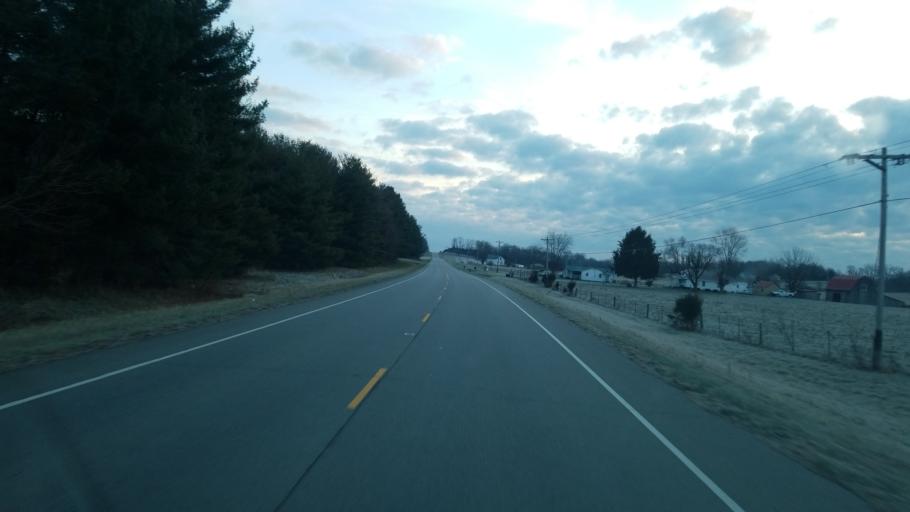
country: US
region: Ohio
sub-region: Highland County
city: Greenfield
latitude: 39.2282
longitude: -83.3760
